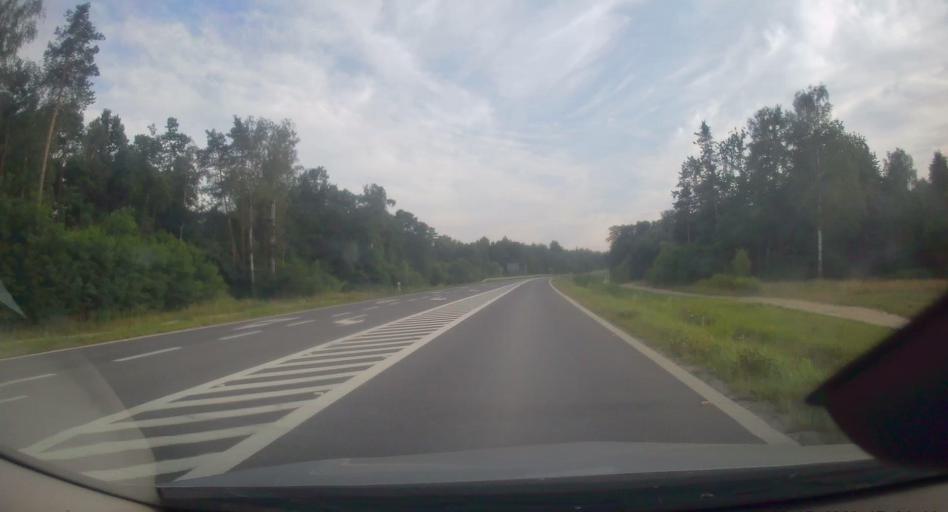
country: PL
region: Lesser Poland Voivodeship
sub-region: Powiat brzeski
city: Przyborow
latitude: 50.0154
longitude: 20.6202
